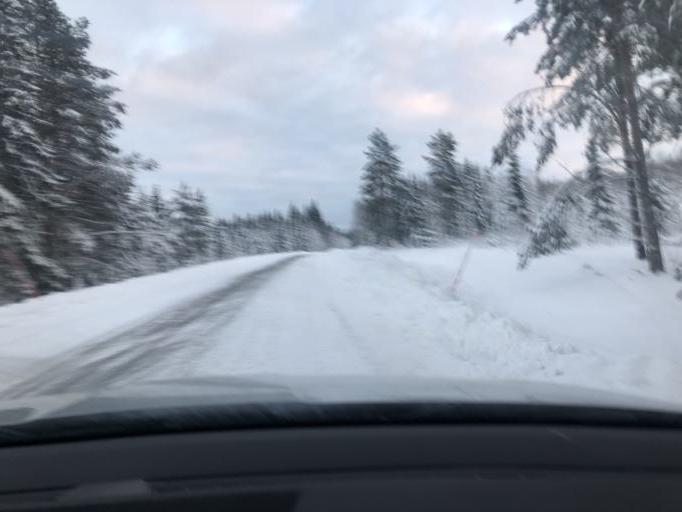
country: SE
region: Vaesternorrland
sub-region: Kramfors Kommun
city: Nordingra
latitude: 62.9973
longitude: 18.2349
